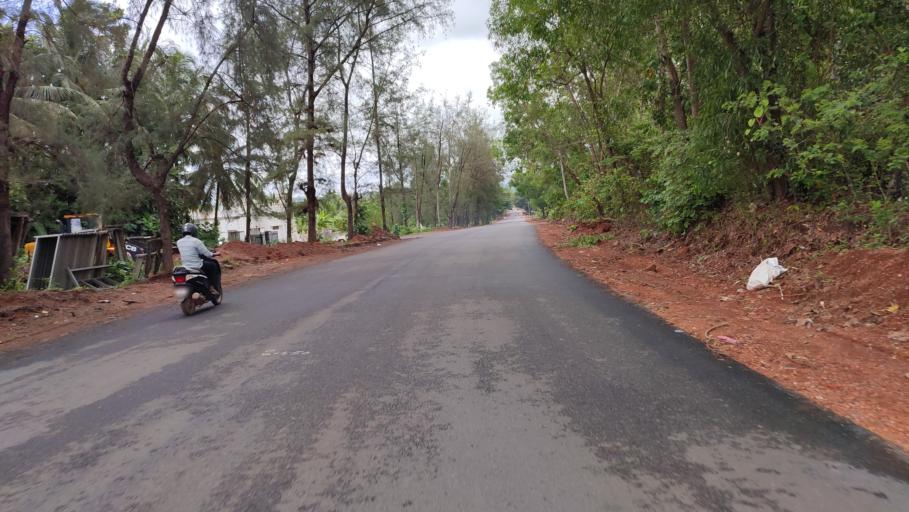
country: IN
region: Kerala
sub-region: Kasaragod District
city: Kasaragod
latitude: 12.5409
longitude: 75.0712
